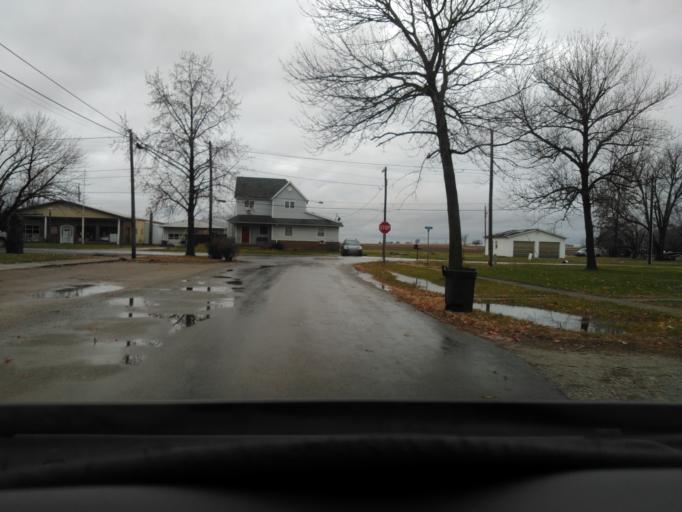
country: US
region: Illinois
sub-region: Effingham County
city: Altamont
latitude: 39.0630
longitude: -88.7559
